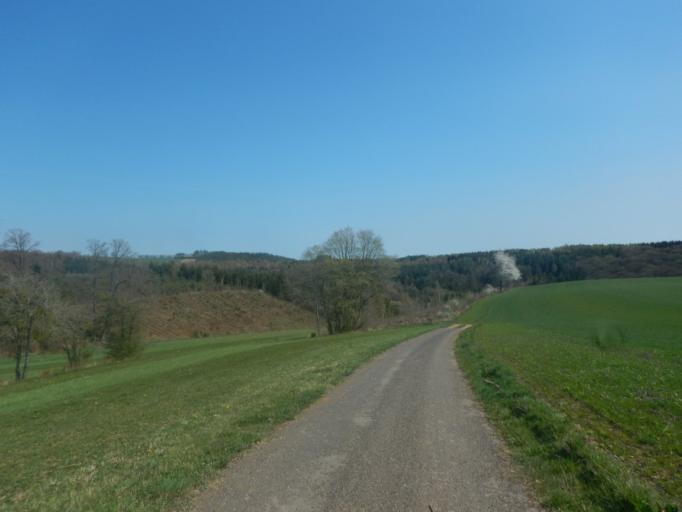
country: LU
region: Diekirch
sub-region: Canton de Clervaux
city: Clervaux
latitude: 50.0457
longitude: 5.9965
